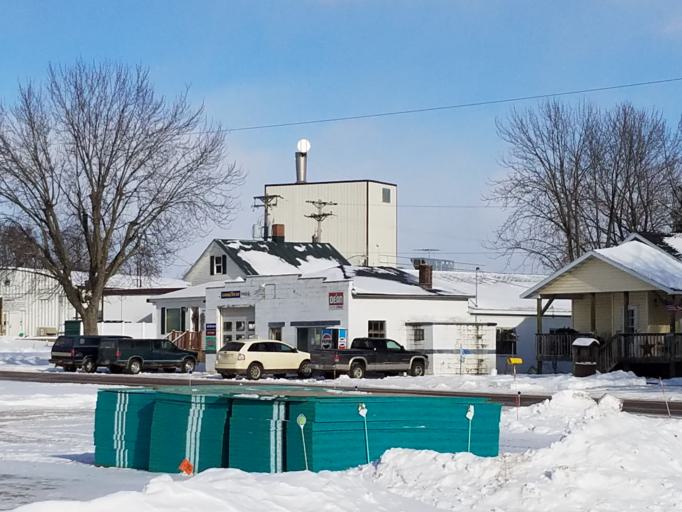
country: US
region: Wisconsin
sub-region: Marathon County
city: Spencer
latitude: 44.6262
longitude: -90.3577
